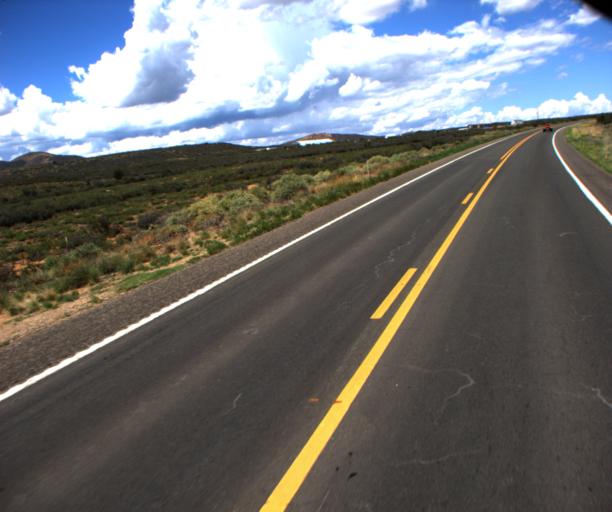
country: US
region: Arizona
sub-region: Yavapai County
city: Dewey-Humboldt
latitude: 34.5359
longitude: -112.1412
